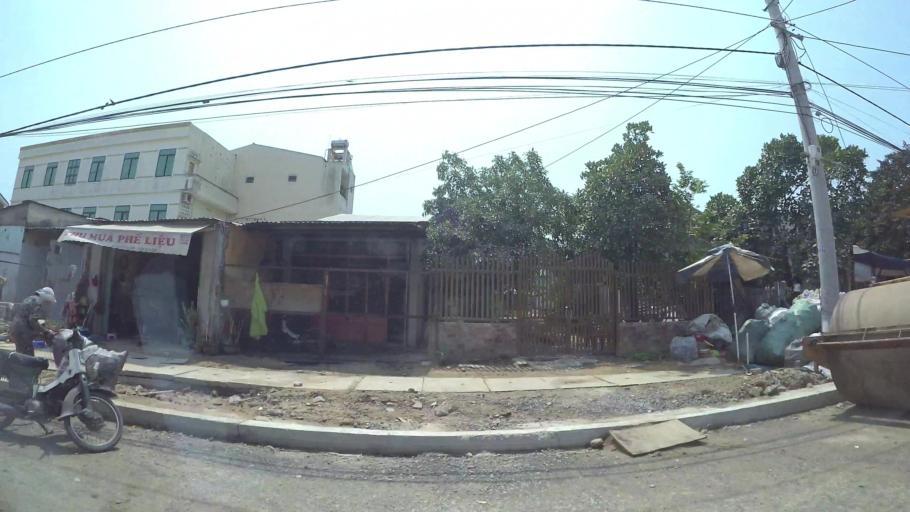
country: VN
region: Da Nang
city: Ngu Hanh Son
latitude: 16.0090
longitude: 108.2562
